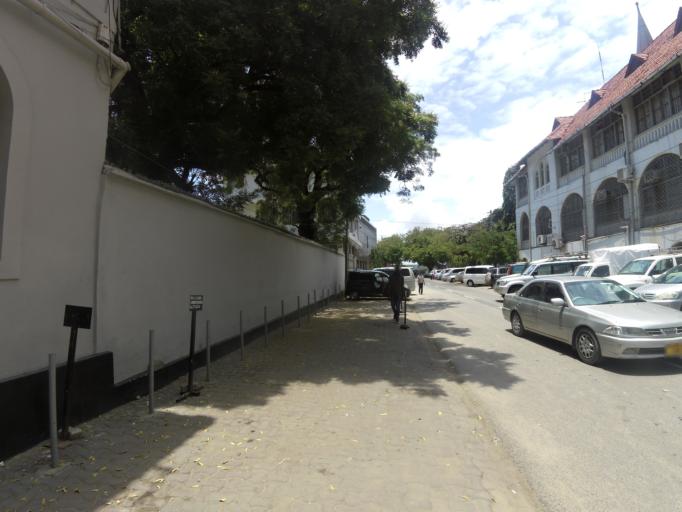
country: TZ
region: Dar es Salaam
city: Dar es Salaam
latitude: -6.8186
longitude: 39.2879
